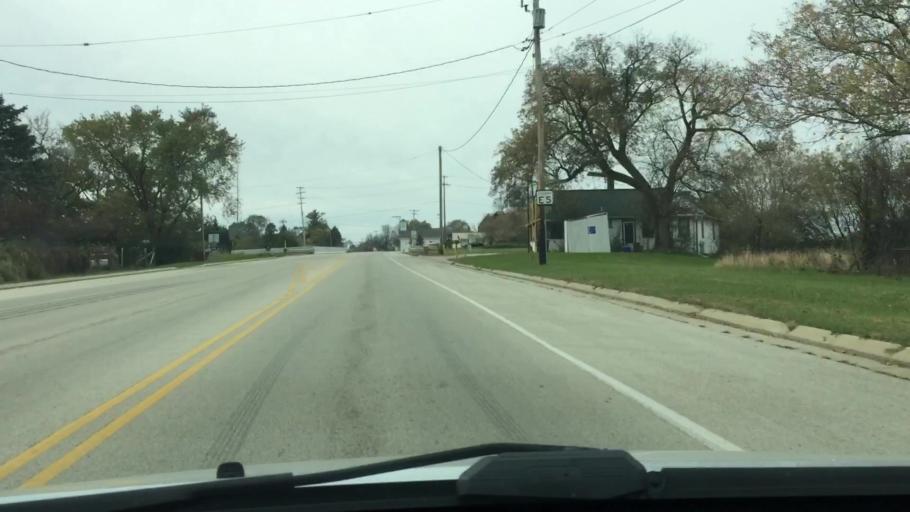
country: US
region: Wisconsin
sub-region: Waukesha County
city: Muskego
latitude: 42.9460
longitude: -88.1570
